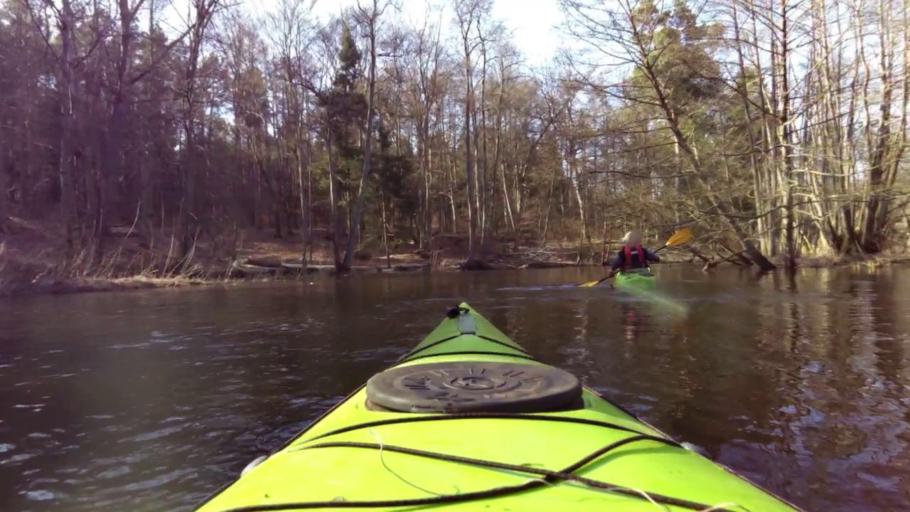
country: PL
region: West Pomeranian Voivodeship
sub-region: Powiat lobeski
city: Lobez
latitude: 53.7075
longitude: 15.5486
